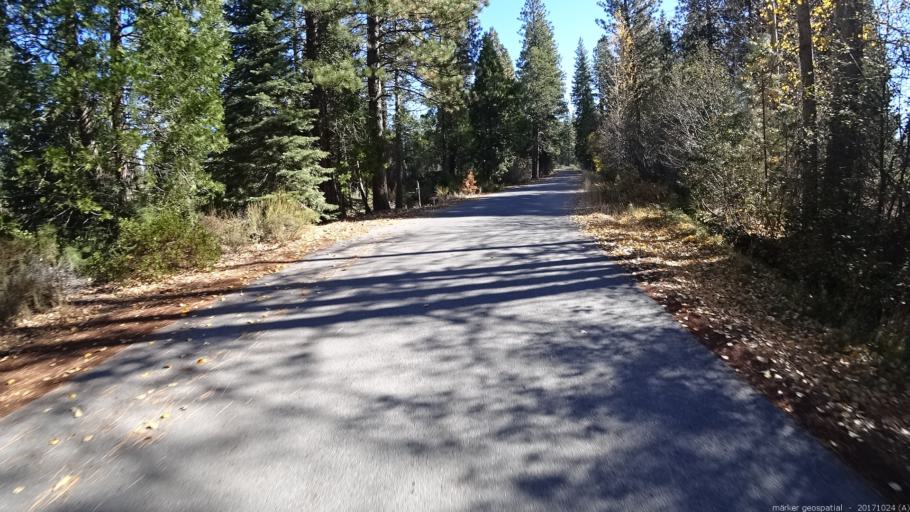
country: US
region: California
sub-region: Shasta County
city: Burney
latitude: 40.7540
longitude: -121.4873
